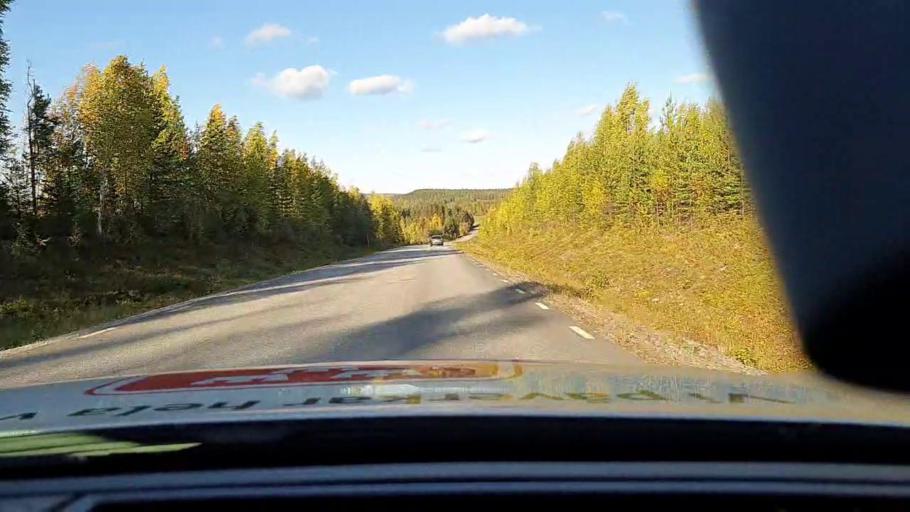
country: SE
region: Norrbotten
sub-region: Pitea Kommun
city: Norrfjarden
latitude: 65.5049
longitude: 21.4797
